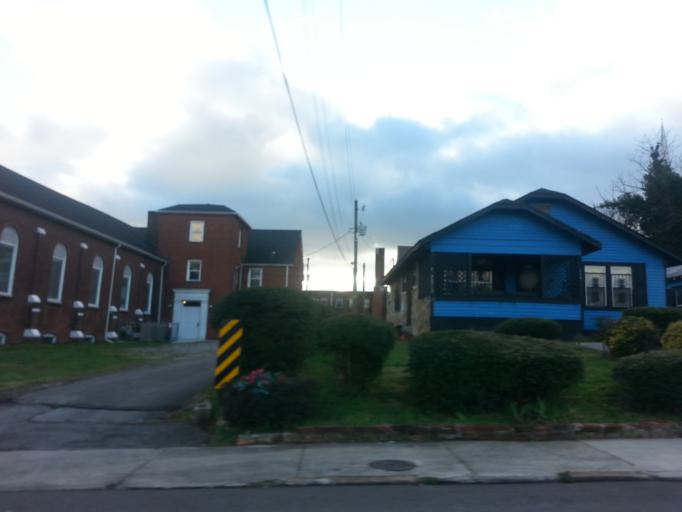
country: US
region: Tennessee
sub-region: Knox County
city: Knoxville
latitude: 35.9979
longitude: -83.8758
